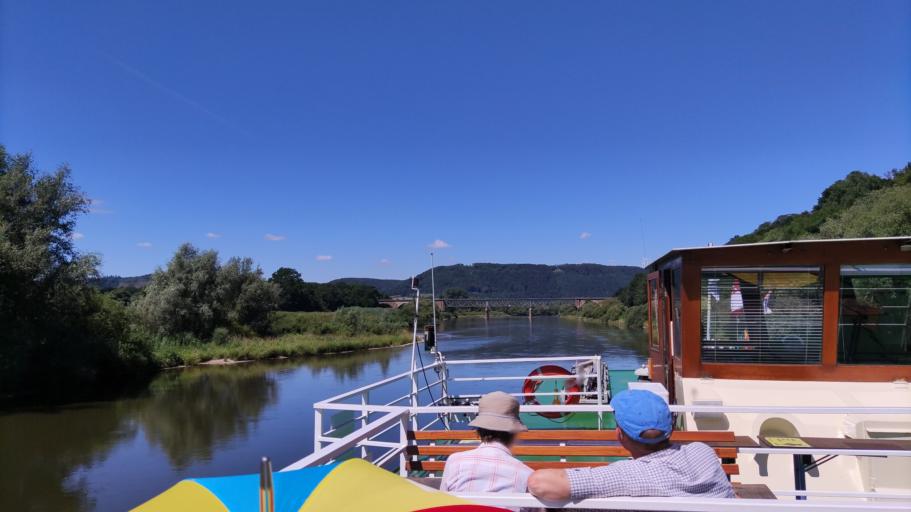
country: DE
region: Lower Saxony
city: Furstenberg
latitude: 51.7341
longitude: 9.3910
